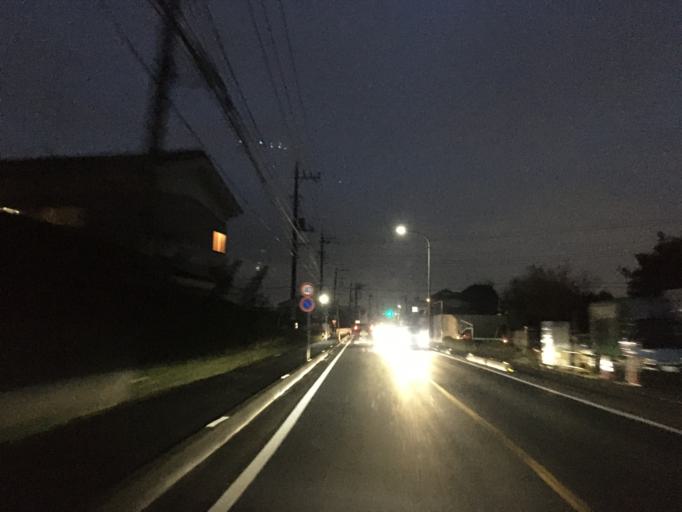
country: JP
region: Saitama
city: Oi
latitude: 35.8025
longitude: 139.5309
